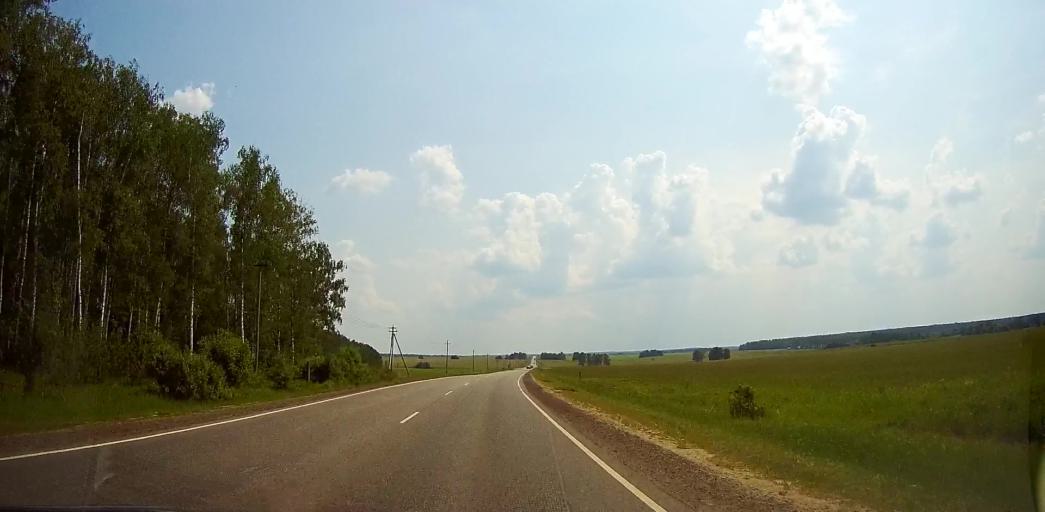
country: RU
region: Moskovskaya
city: Malino
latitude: 55.0528
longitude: 38.1432
